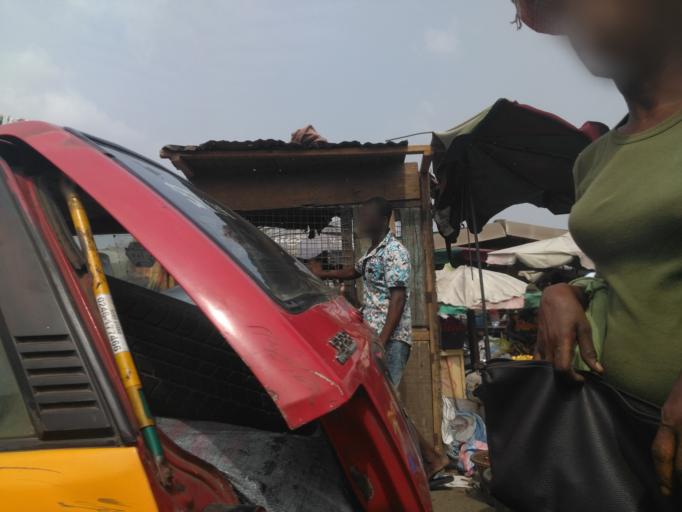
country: GH
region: Greater Accra
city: Accra
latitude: 5.5506
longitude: -0.2208
